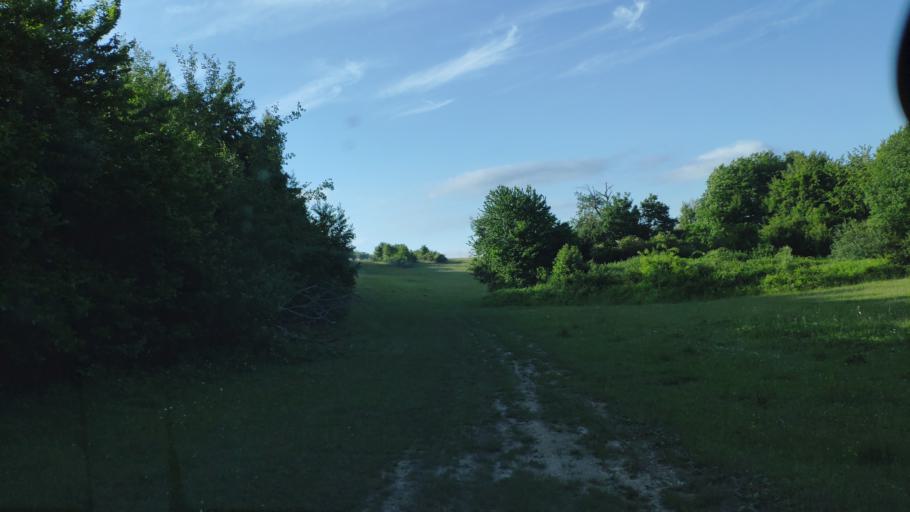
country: SK
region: Presovsky
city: Vranov nad Topl'ou
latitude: 48.8195
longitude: 21.5886
